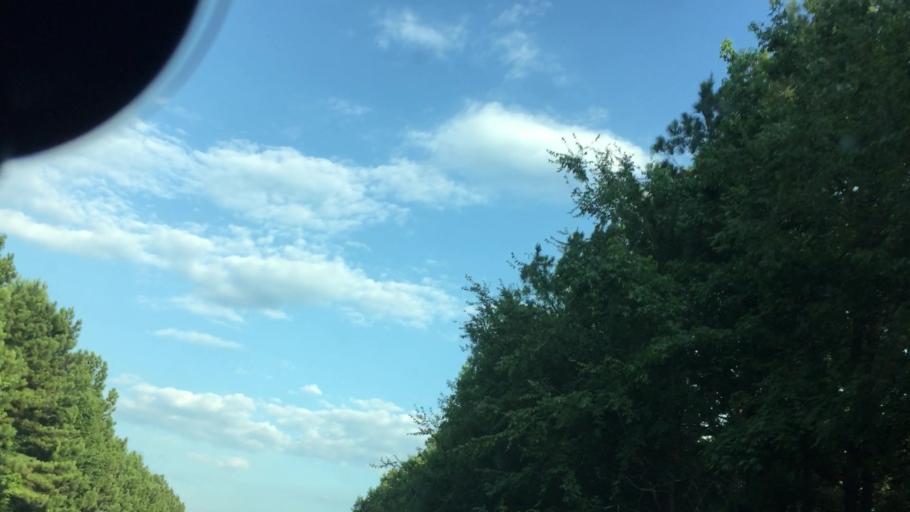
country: US
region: Georgia
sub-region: DeKalb County
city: Pine Mountain
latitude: 33.6603
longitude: -84.1915
